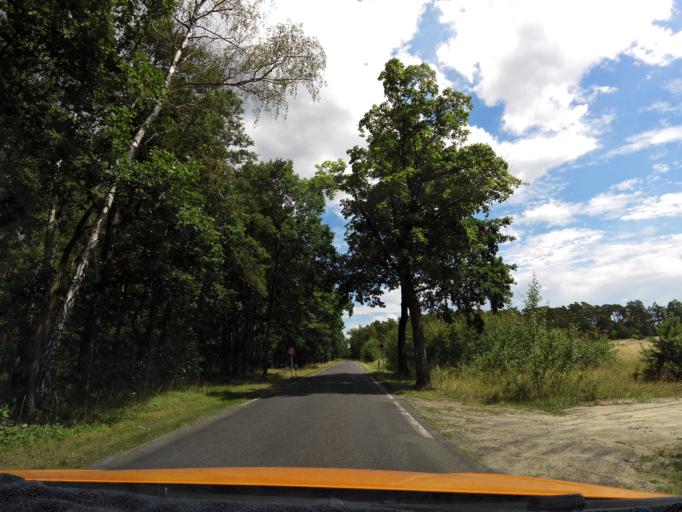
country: DE
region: Brandenburg
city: Storkow
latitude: 52.2467
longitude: 13.8685
